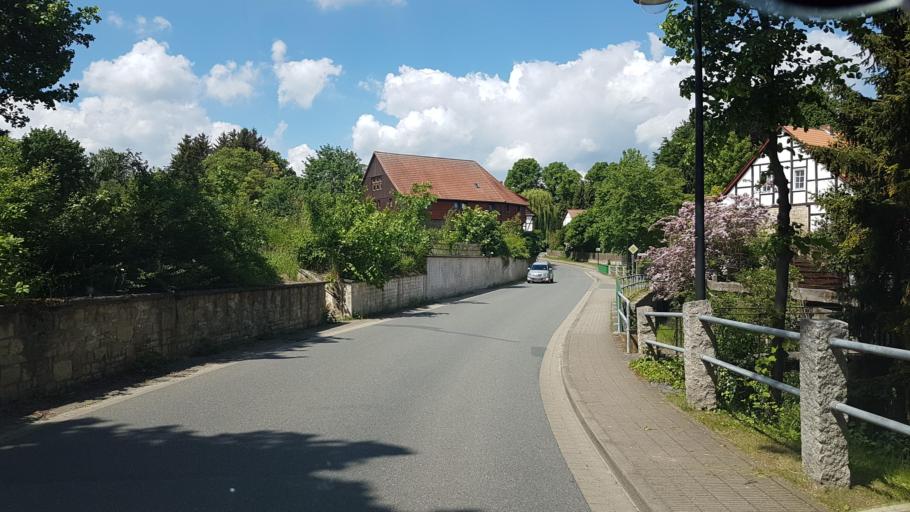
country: DE
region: Lower Saxony
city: Rabke
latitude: 52.1947
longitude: 10.8784
